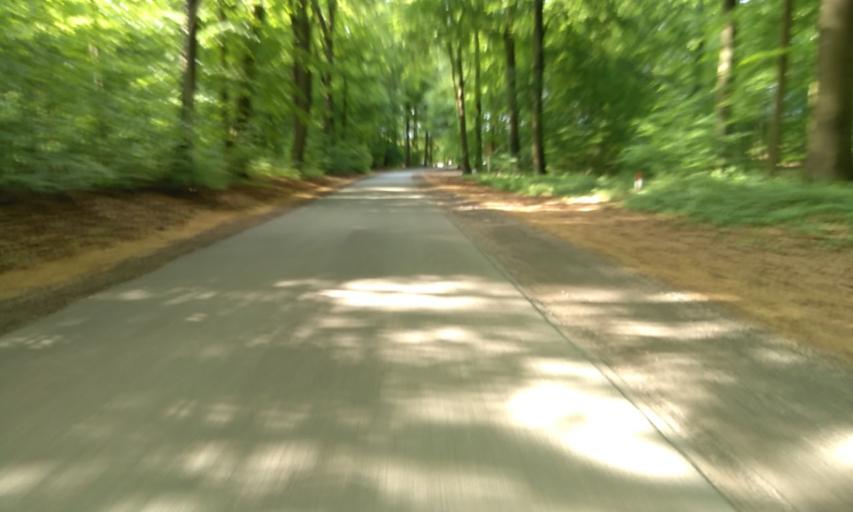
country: DE
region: Lower Saxony
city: Nottensdorf
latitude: 53.4774
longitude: 9.6365
